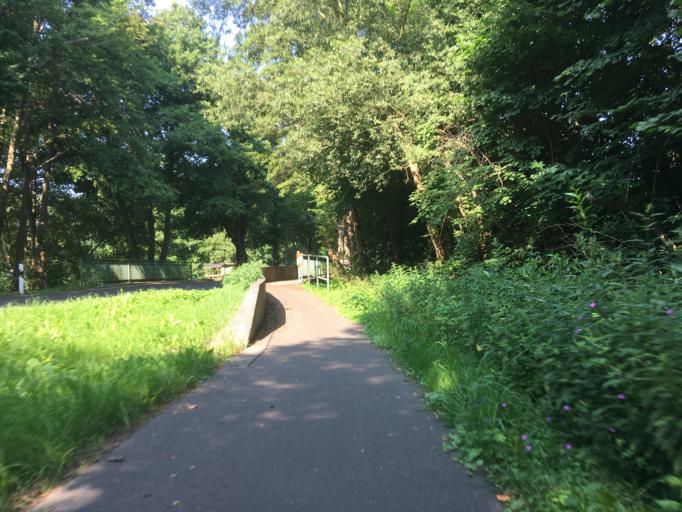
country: DE
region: Brandenburg
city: Borkwalde
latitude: 52.3026
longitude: 12.7703
